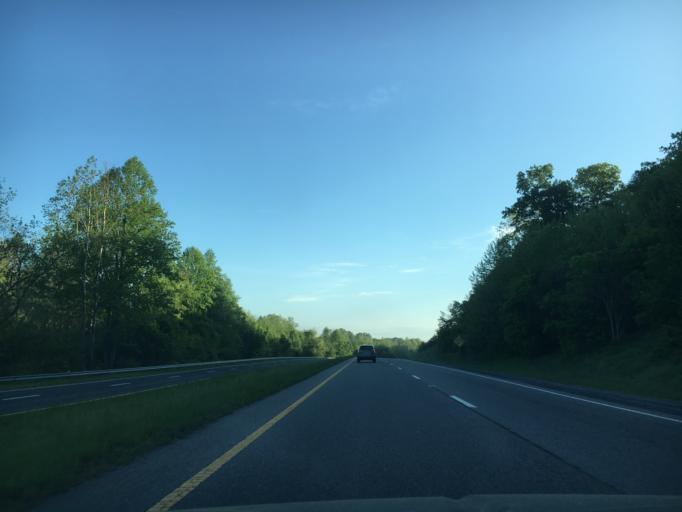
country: US
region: Virginia
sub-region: Campbell County
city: Rustburg
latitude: 37.3093
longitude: -79.1085
